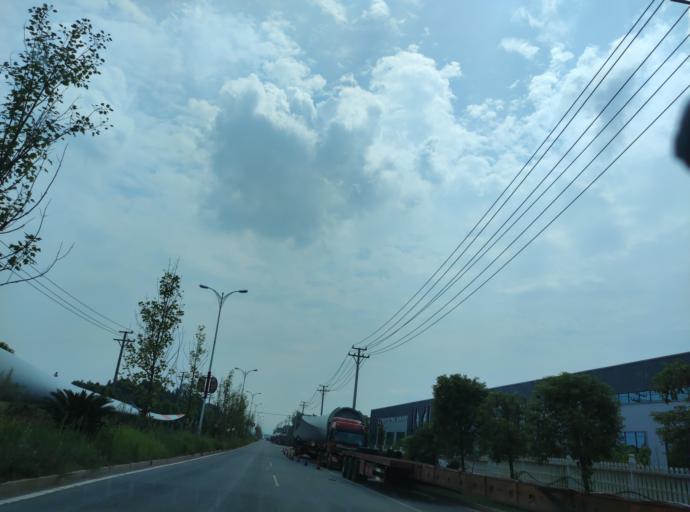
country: CN
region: Jiangxi Sheng
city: Yuannan
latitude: 27.6640
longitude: 114.0228
